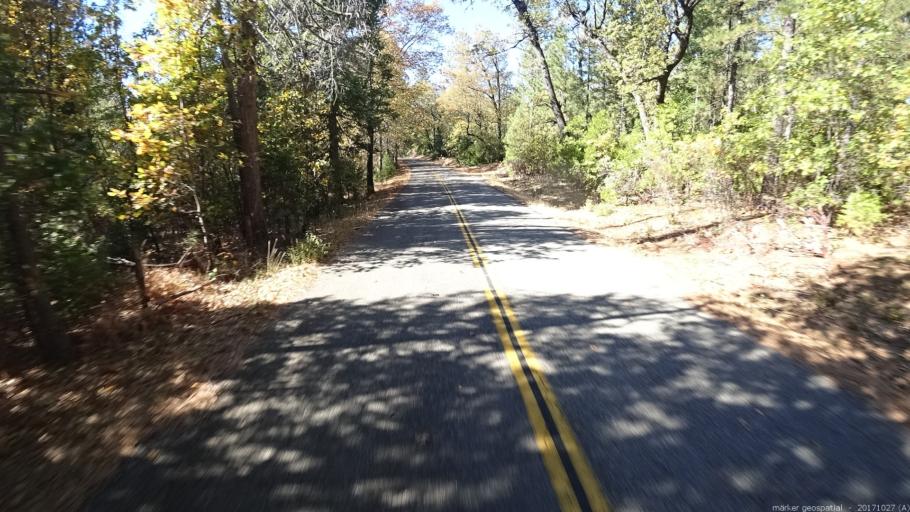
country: US
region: California
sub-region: Shasta County
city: Bella Vista
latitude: 40.7177
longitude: -121.9964
